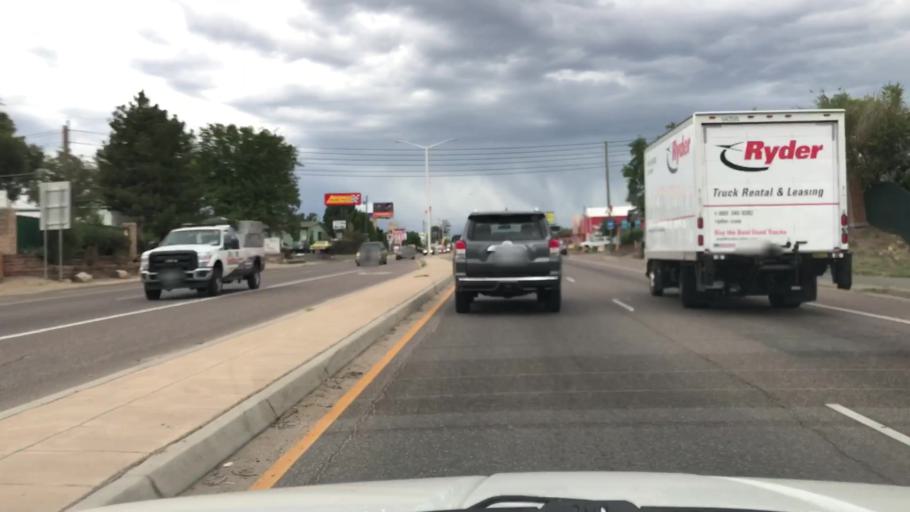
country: US
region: Colorado
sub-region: Adams County
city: Berkley
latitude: 39.7978
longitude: -105.0254
